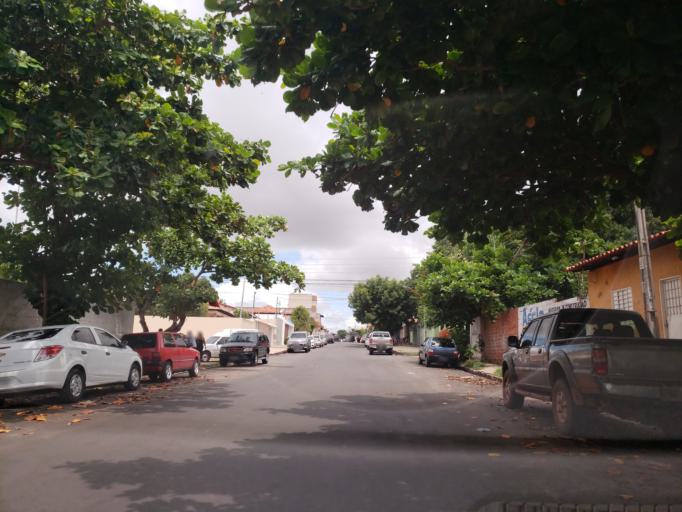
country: BR
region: Piaui
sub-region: Teresina
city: Teresina
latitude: -5.1093
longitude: -42.8110
